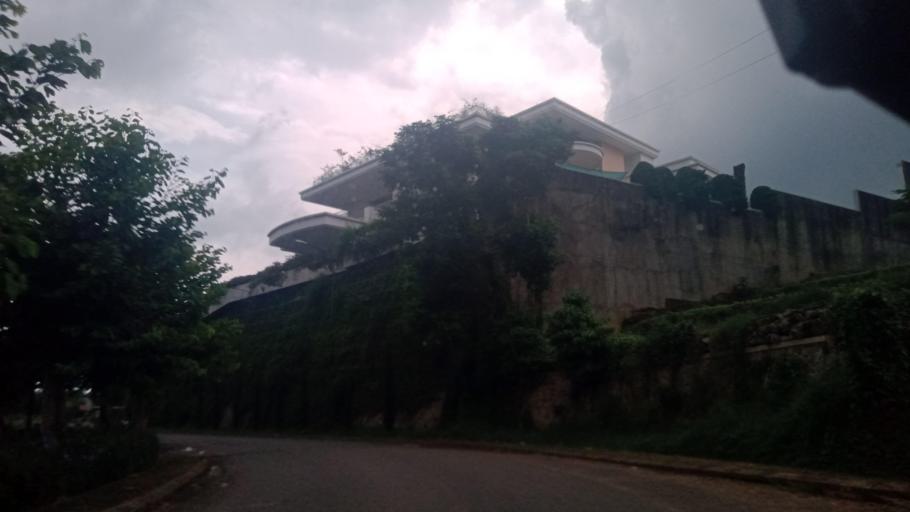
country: ID
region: West Java
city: Lembang
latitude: -6.8493
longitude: 107.5892
